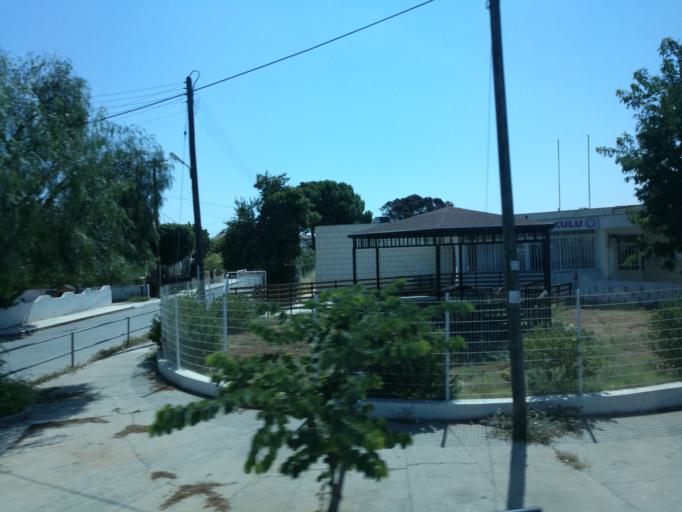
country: CY
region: Ammochostos
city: Famagusta
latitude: 35.1134
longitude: 33.9427
